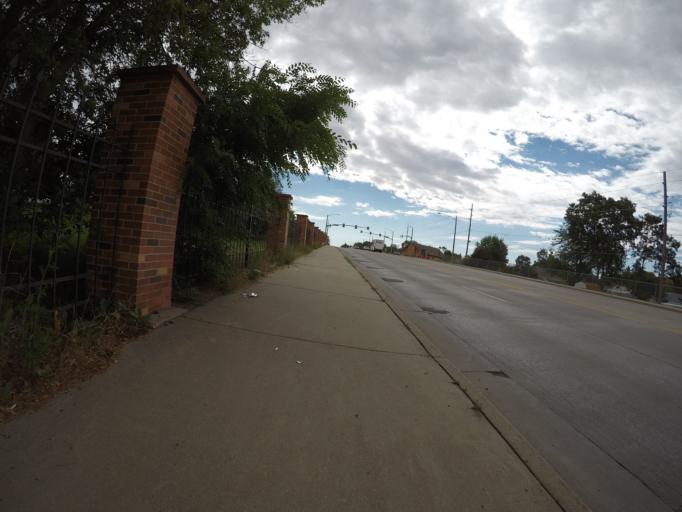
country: US
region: Wyoming
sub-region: Laramie County
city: Fox Farm-College
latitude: 41.1458
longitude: -104.7868
